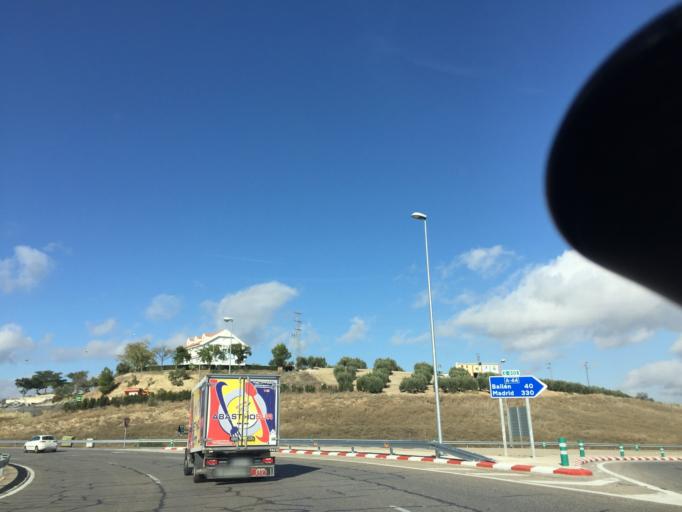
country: ES
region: Andalusia
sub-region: Provincia de Jaen
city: Jaen
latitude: 37.7822
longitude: -3.7557
